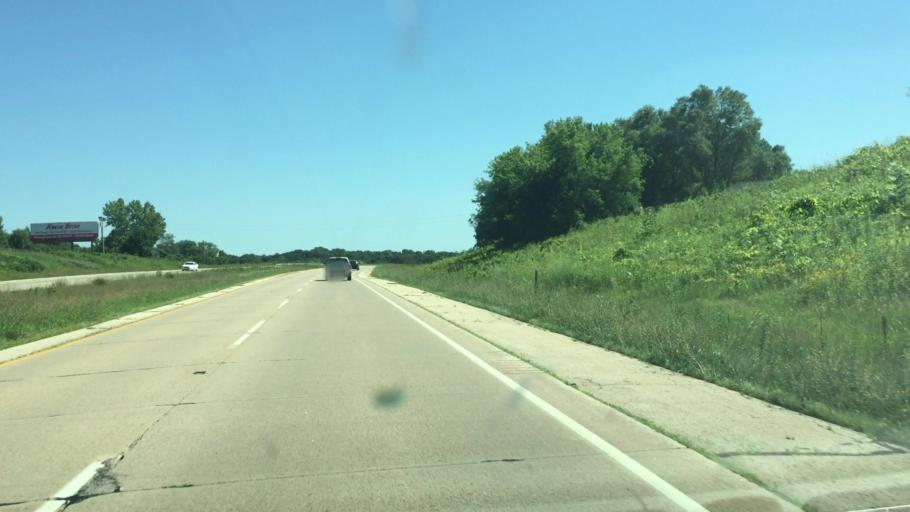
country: US
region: Illinois
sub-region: Jo Daviess County
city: East Dubuque
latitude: 42.5472
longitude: -90.6086
